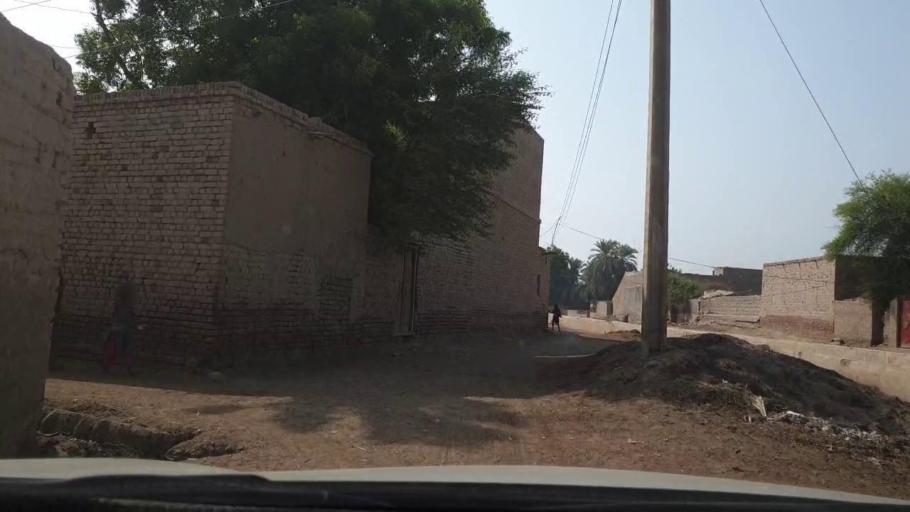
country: PK
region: Sindh
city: Larkana
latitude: 27.4659
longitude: 68.2431
